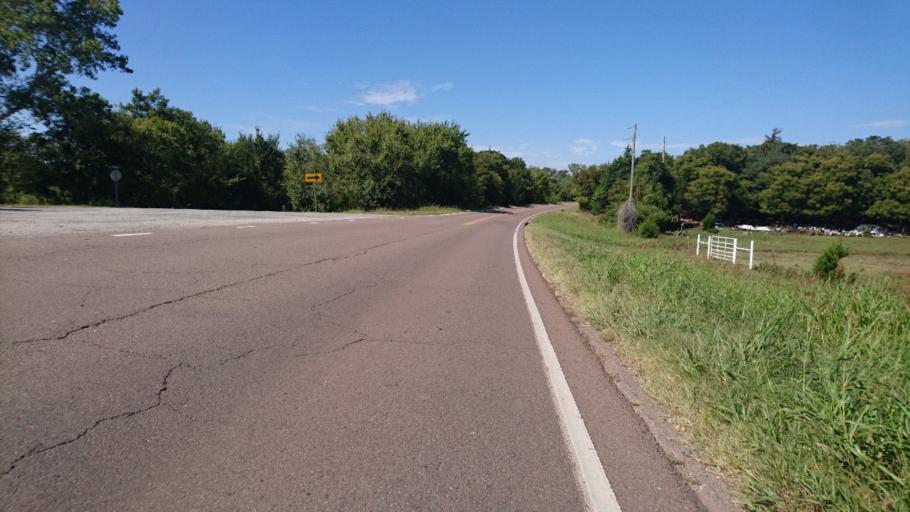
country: US
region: Oklahoma
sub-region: Oklahoma County
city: Jones
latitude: 35.6599
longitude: -97.2897
